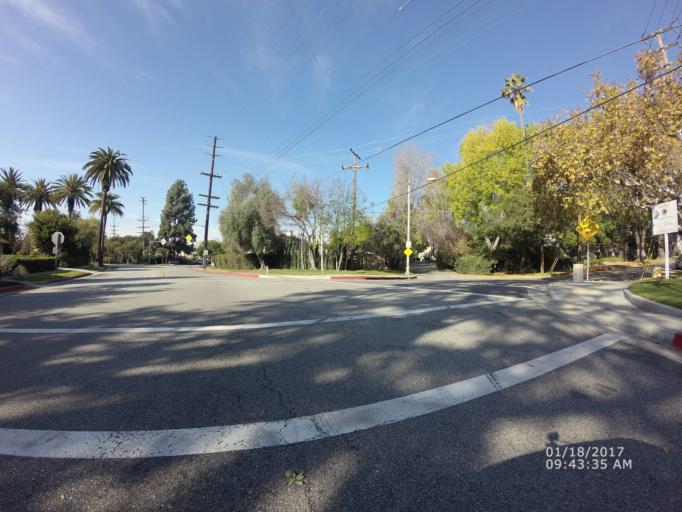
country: US
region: California
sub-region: Los Angeles County
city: South Pasadena
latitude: 34.1191
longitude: -118.1451
